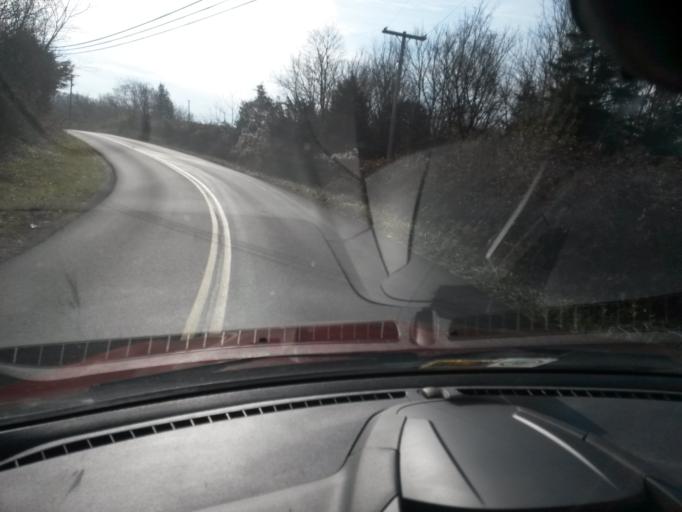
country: US
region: Virginia
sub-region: Botetourt County
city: Fincastle
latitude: 37.5238
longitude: -79.8819
